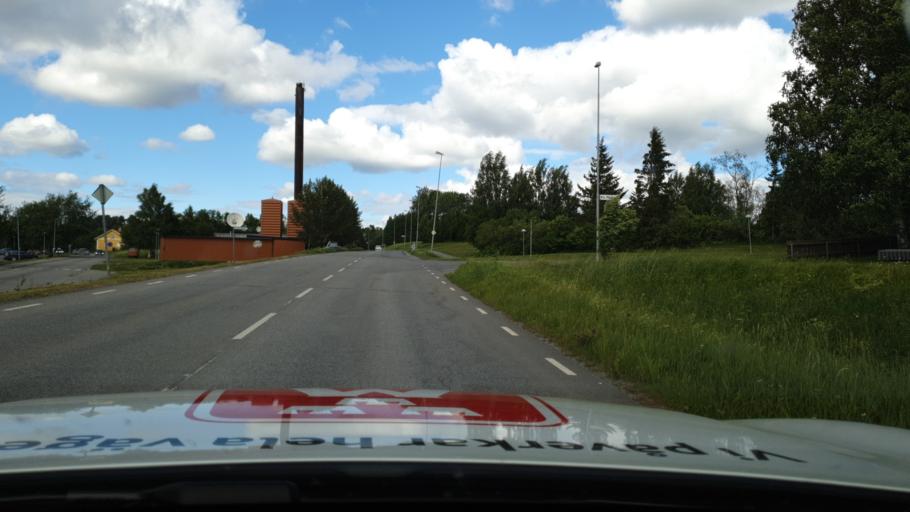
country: SE
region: Jaemtland
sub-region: OEstersunds Kommun
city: Brunflo
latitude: 63.0748
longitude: 14.8206
